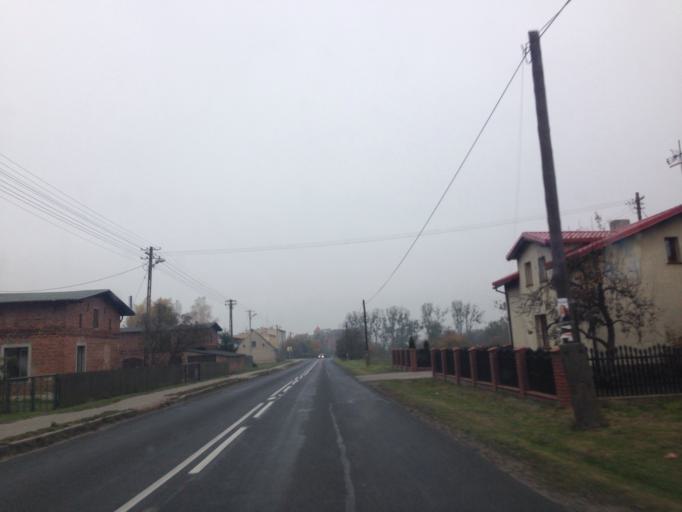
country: PL
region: Kujawsko-Pomorskie
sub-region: Powiat brodnicki
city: Brodnica
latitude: 53.2441
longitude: 19.4670
